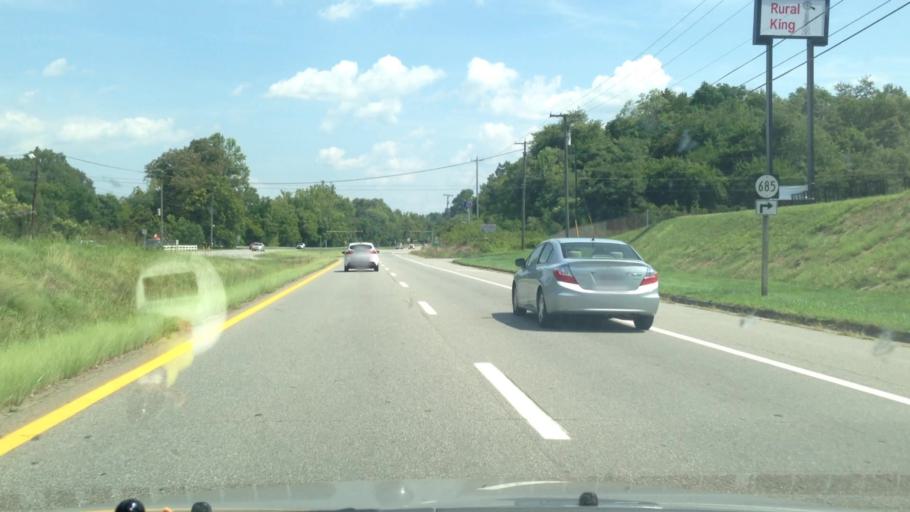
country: US
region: Virginia
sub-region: City of Martinsville
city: Martinsville
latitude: 36.6522
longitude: -79.8730
